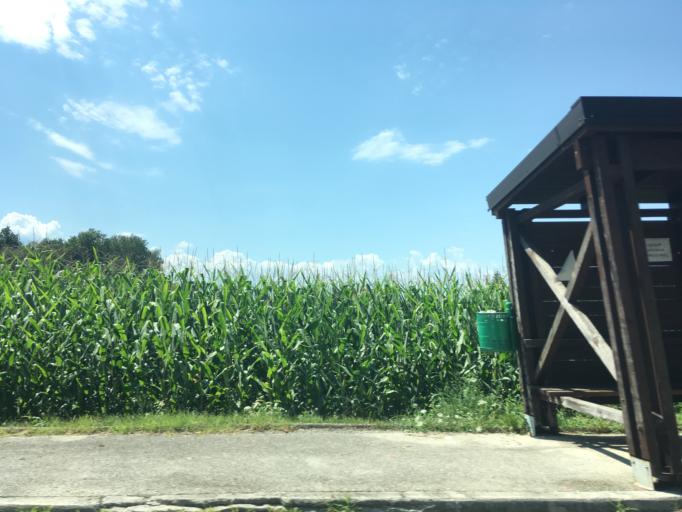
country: SI
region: Metlika
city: Metlika
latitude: 45.6158
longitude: 15.3244
